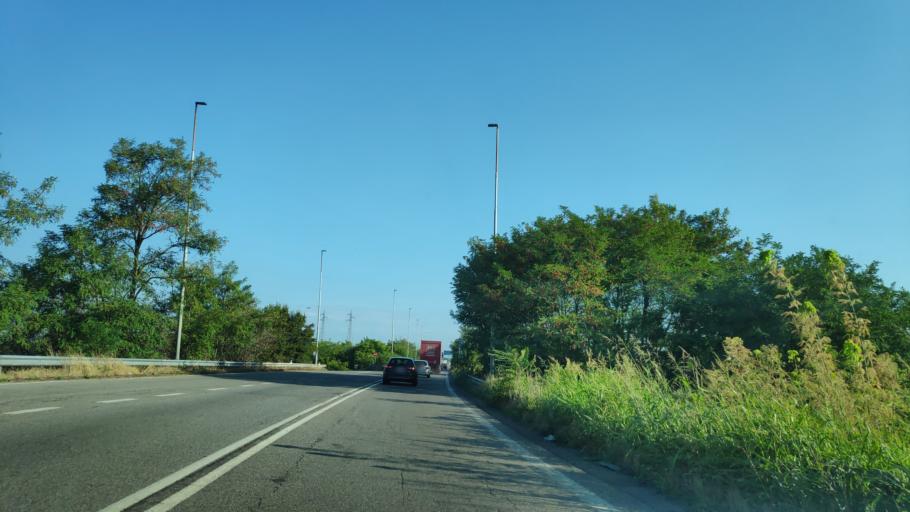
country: IT
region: Lombardy
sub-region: Citta metropolitana di Milano
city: Locate di Triulzi
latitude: 45.3694
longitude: 9.2275
